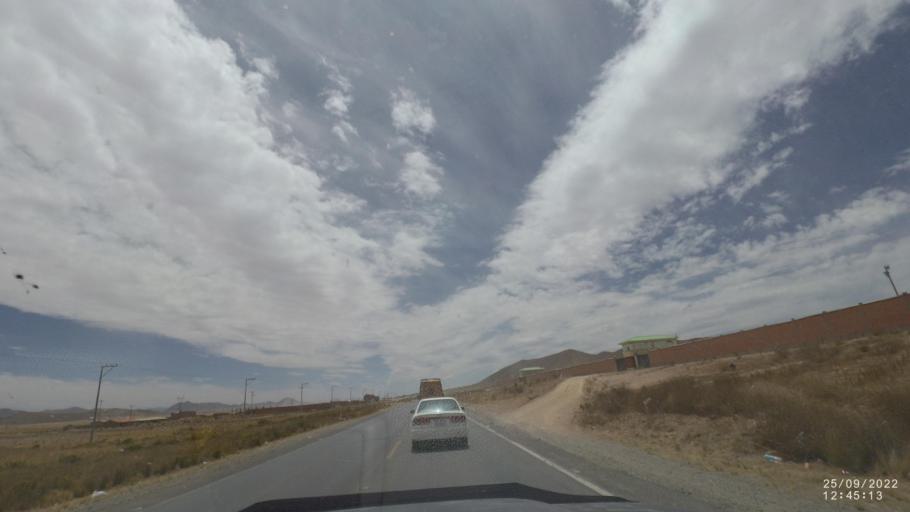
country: BO
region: Oruro
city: Machacamarca
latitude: -18.0470
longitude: -67.0121
